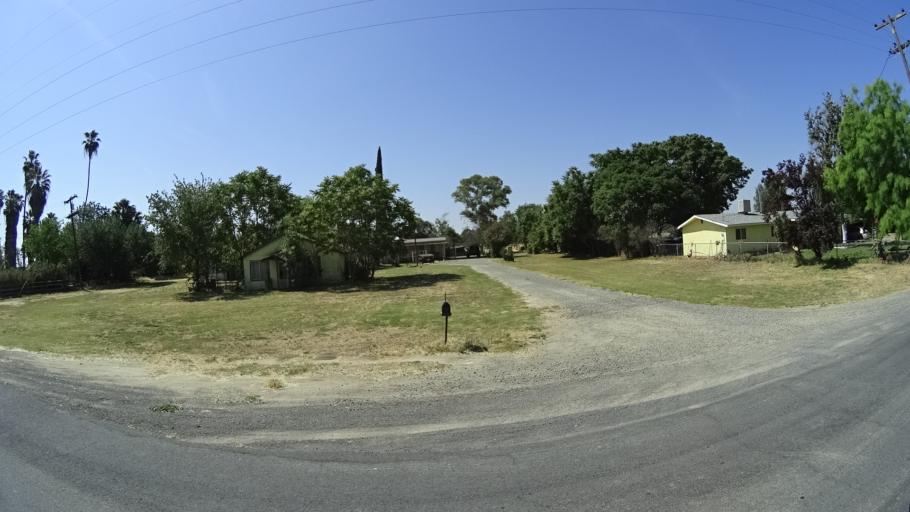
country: US
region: California
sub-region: Kings County
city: Lemoore
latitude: 36.3280
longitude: -119.8177
